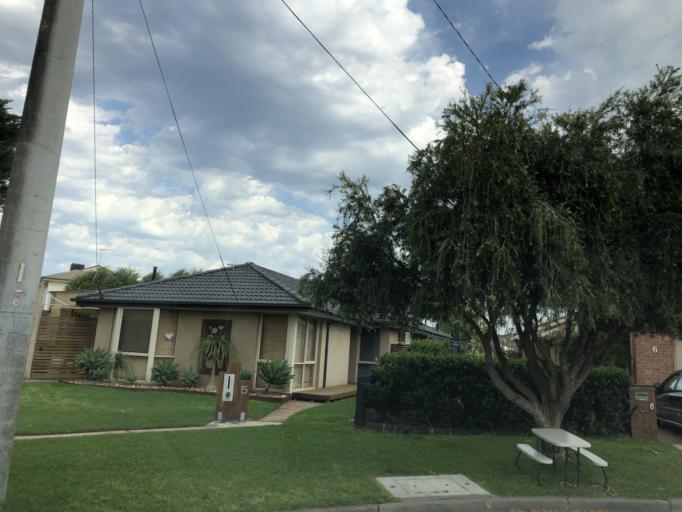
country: AU
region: Victoria
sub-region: Kingston
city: Carrum
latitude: -38.0871
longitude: 145.1349
